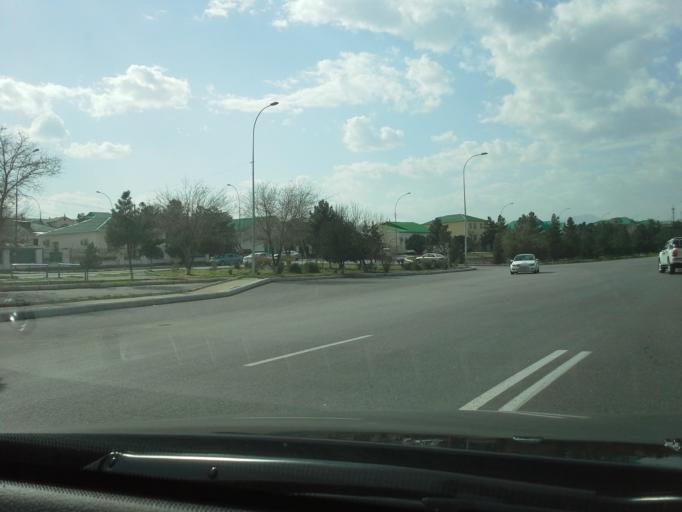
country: TM
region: Ahal
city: Ashgabat
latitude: 37.9582
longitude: 58.3208
